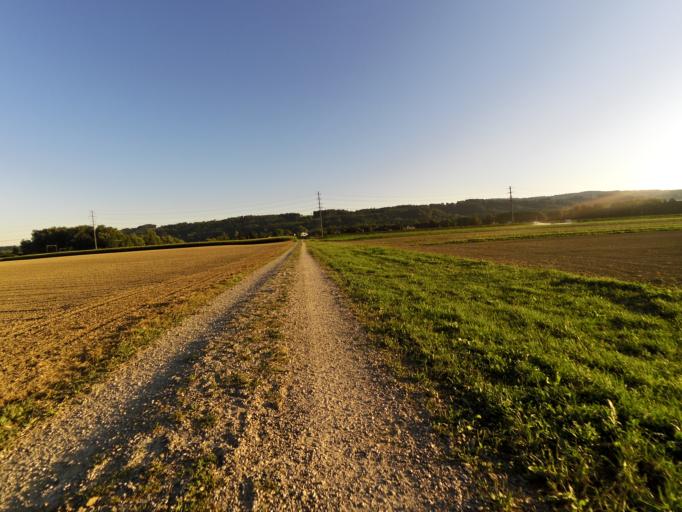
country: CH
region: Thurgau
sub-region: Weinfelden District
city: Wigoltingen
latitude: 47.5896
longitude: 9.0260
